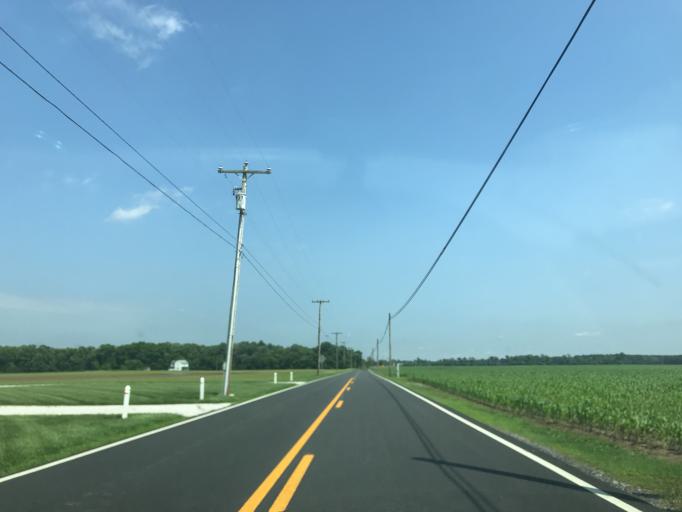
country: US
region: Maryland
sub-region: Dorchester County
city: Hurlock
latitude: 38.5751
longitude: -75.8146
